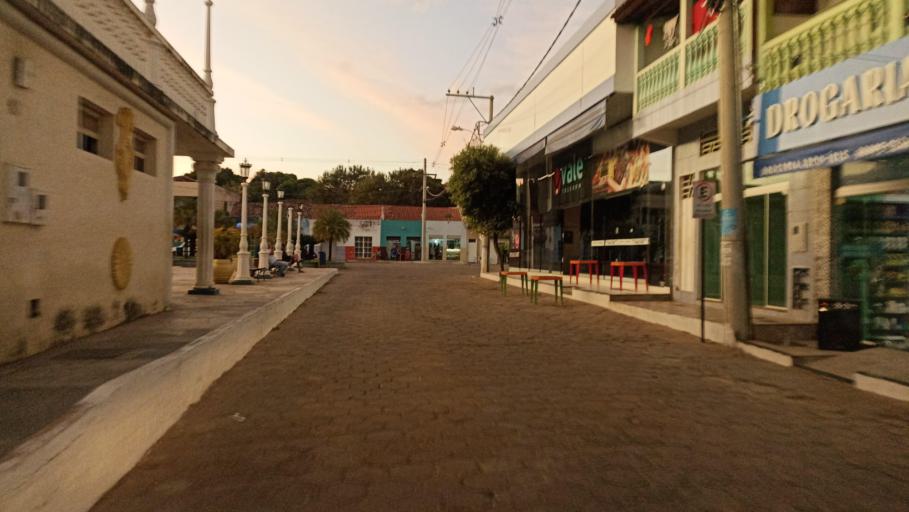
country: BR
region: Minas Gerais
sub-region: Aracuai
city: Aracuai
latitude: -16.6175
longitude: -42.1827
